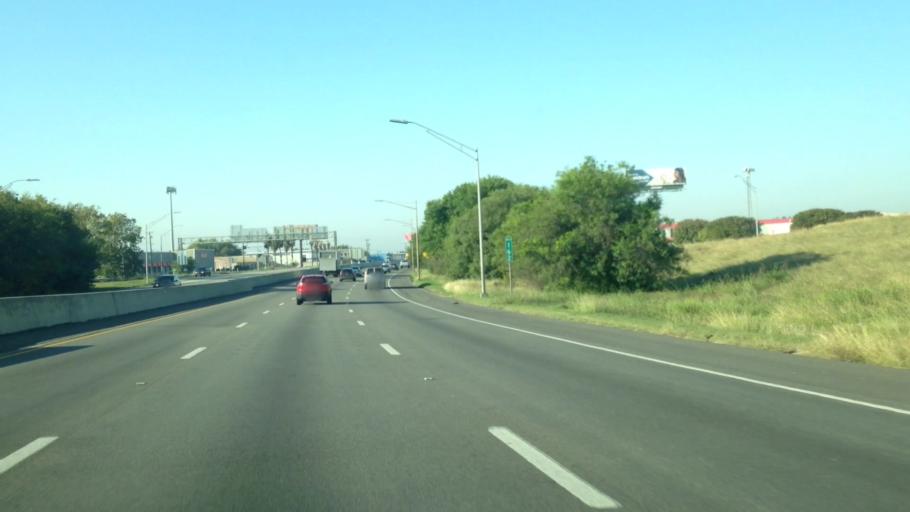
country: US
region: Texas
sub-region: Bexar County
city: Kirby
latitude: 29.4548
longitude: -98.4147
